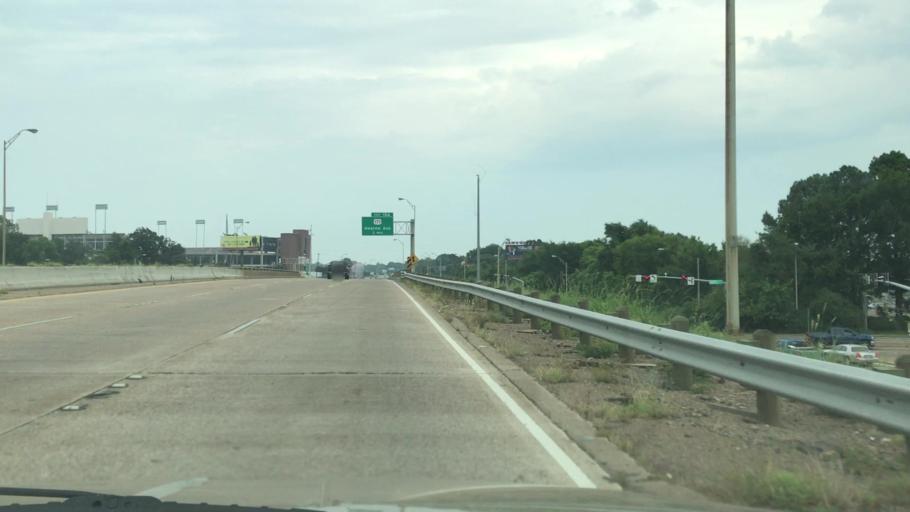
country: US
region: Louisiana
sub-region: Caddo Parish
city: Shreveport
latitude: 32.4719
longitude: -93.7981
